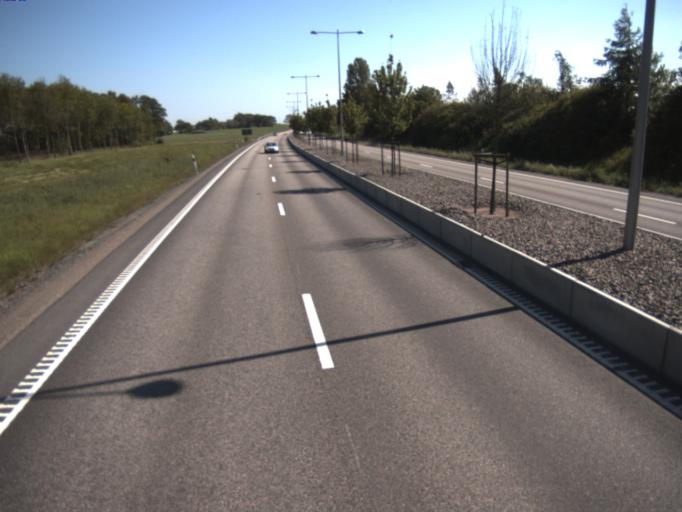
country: SE
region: Skane
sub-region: Helsingborg
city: Odakra
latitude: 56.0479
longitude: 12.7552
